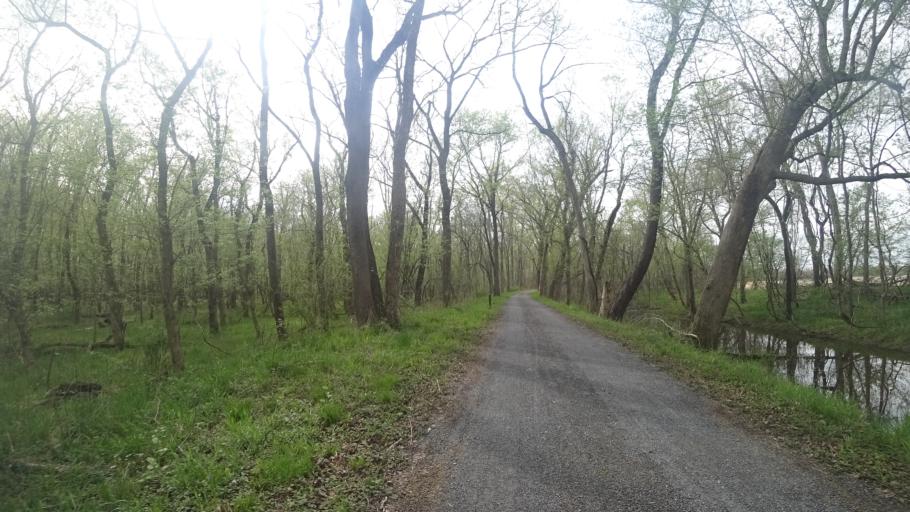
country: US
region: Virginia
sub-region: Loudoun County
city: Leesburg
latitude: 39.1225
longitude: -77.5093
